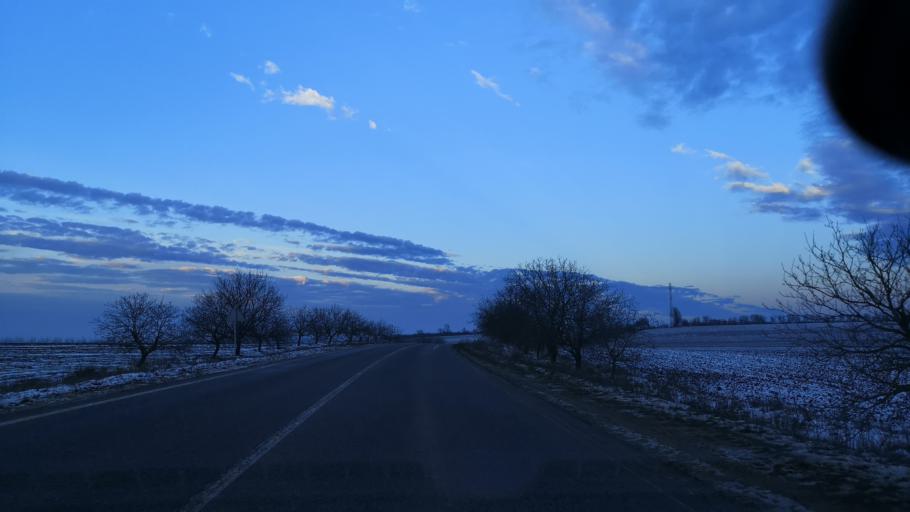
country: MD
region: Orhei
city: Orhei
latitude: 47.5770
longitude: 28.8023
